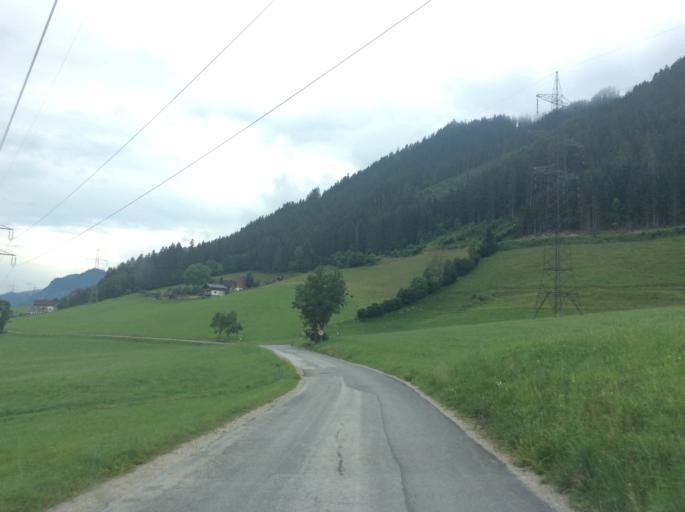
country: AT
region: Styria
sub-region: Politischer Bezirk Liezen
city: Schladming
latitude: 47.3924
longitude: 13.6626
